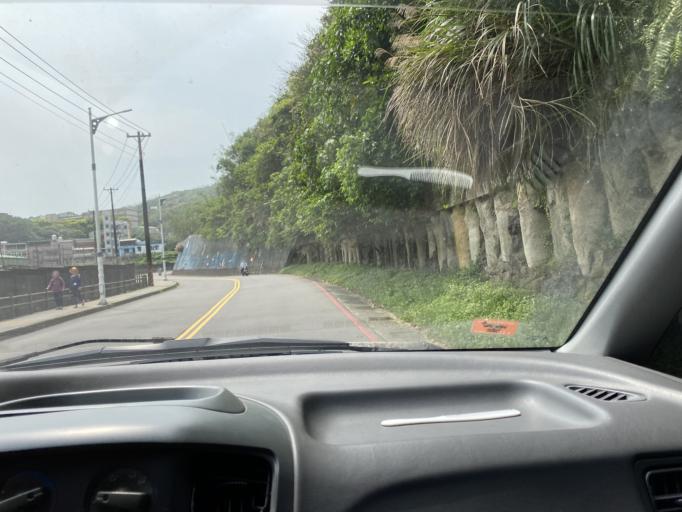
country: TW
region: Taiwan
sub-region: Keelung
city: Keelung
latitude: 25.1575
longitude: 121.7313
